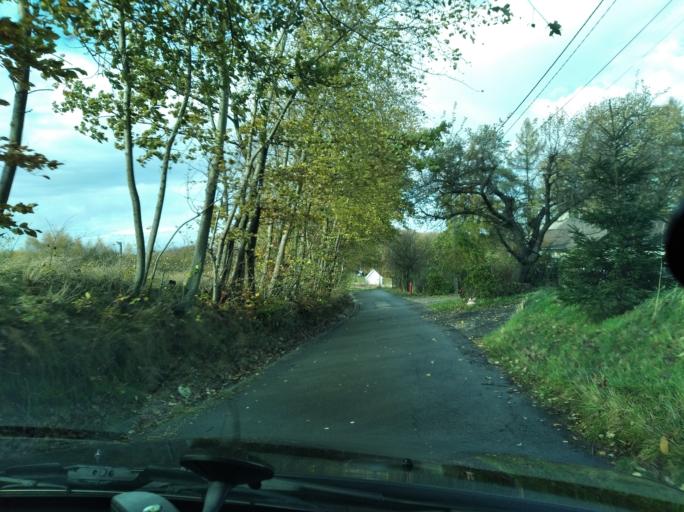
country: PL
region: Subcarpathian Voivodeship
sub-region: Powiat debicki
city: Debica
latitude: 50.0294
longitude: 21.4605
